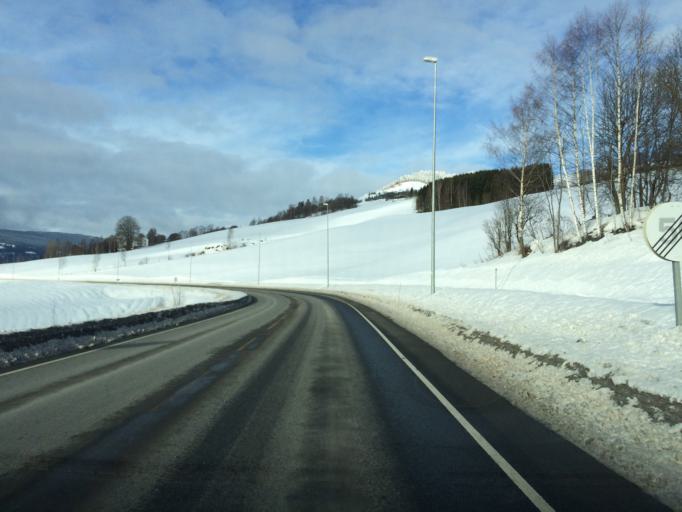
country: NO
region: Oppland
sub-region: Gausdal
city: Segalstad bru
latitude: 61.2197
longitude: 10.2692
